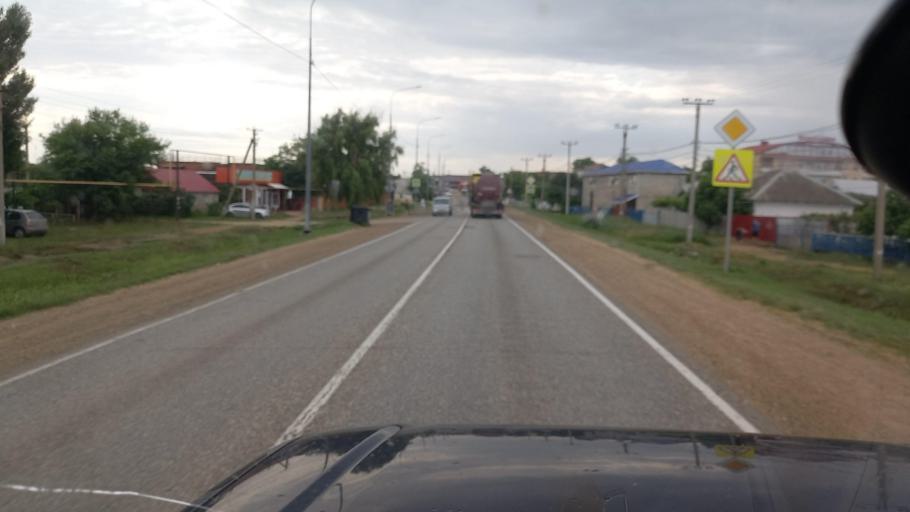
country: RU
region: Krasnodarskiy
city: Akhtanizovskaya
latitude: 45.3477
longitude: 37.1368
